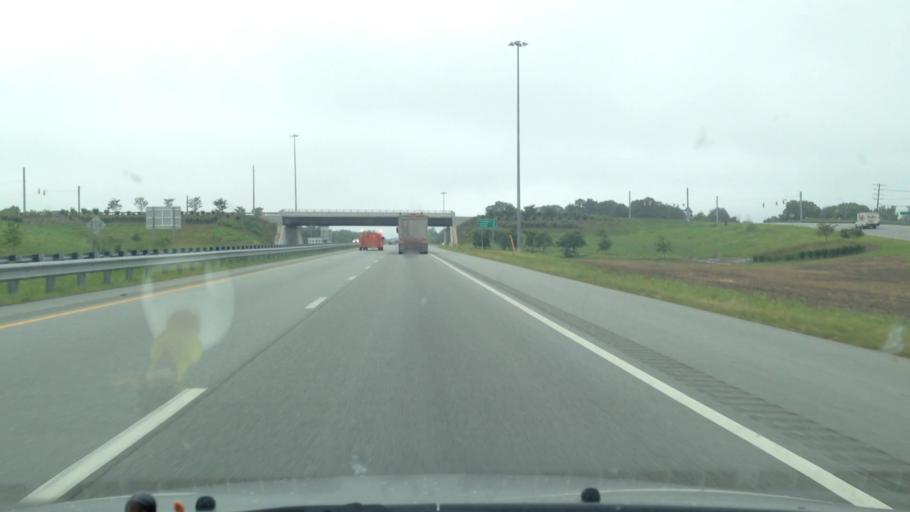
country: US
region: North Carolina
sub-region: Forsyth County
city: Kernersville
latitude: 36.1071
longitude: -80.0490
